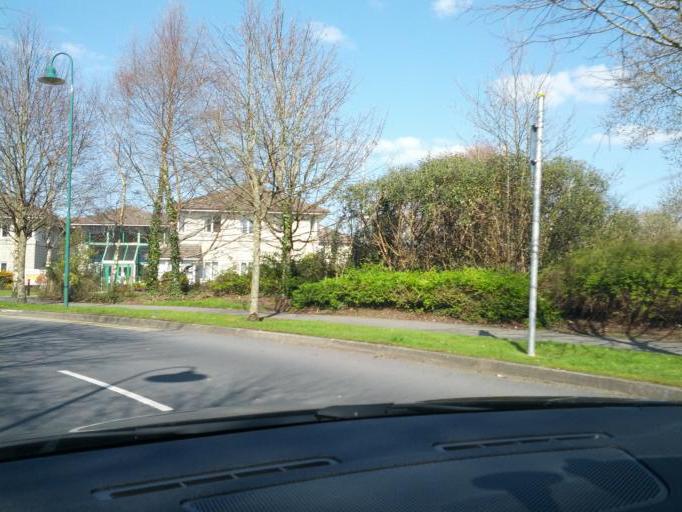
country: IE
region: Connaught
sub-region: County Galway
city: Gaillimh
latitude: 53.2898
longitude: -9.0736
